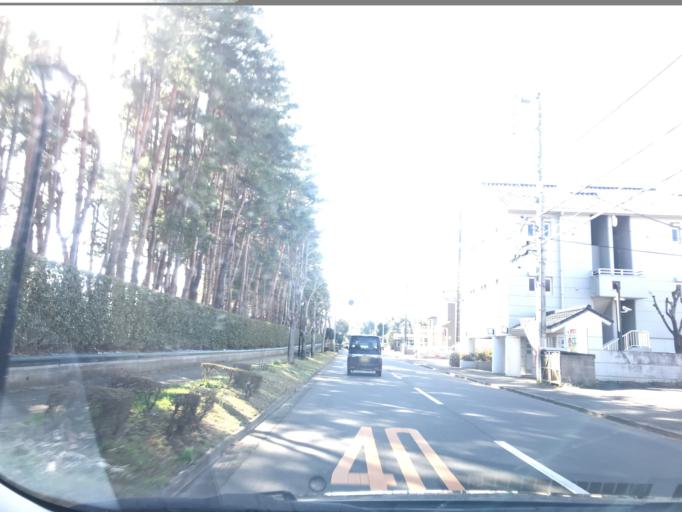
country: JP
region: Ibaraki
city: Tsukuba
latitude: 36.1278
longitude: 140.0885
